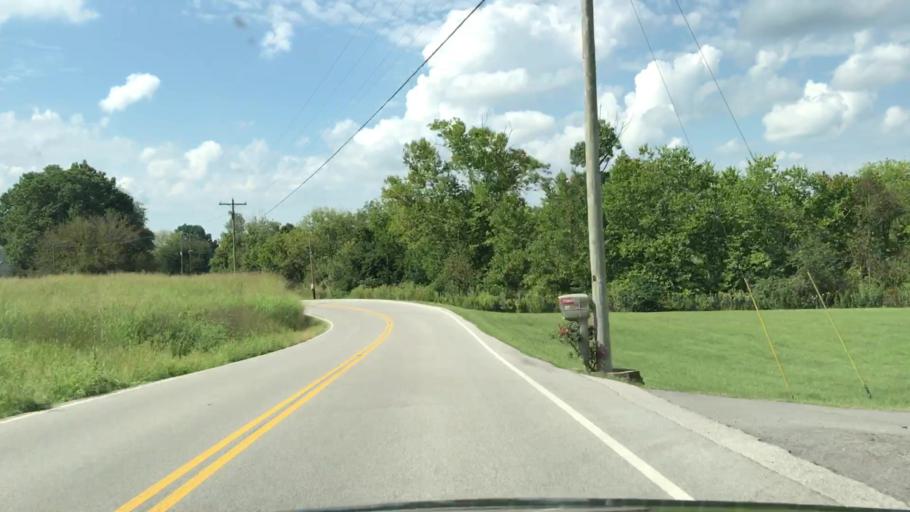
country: US
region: Tennessee
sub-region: Trousdale County
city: Hartsville
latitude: 36.4522
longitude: -86.1789
